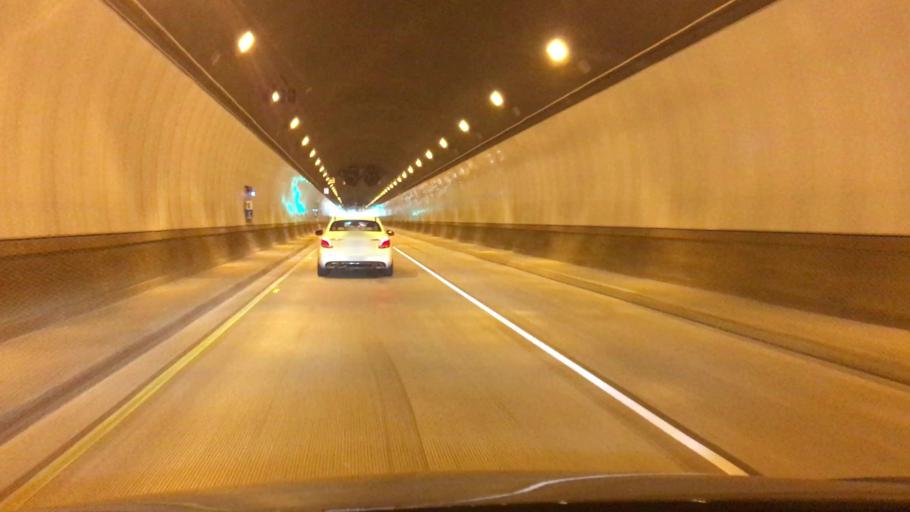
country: US
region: California
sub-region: San Mateo County
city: Montara
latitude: 37.5801
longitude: -122.5116
